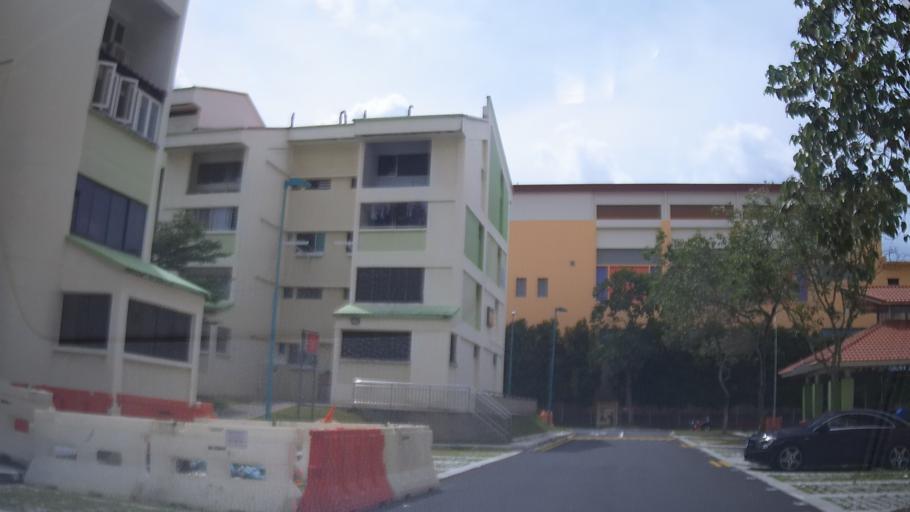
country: SG
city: Singapore
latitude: 1.3499
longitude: 103.8866
